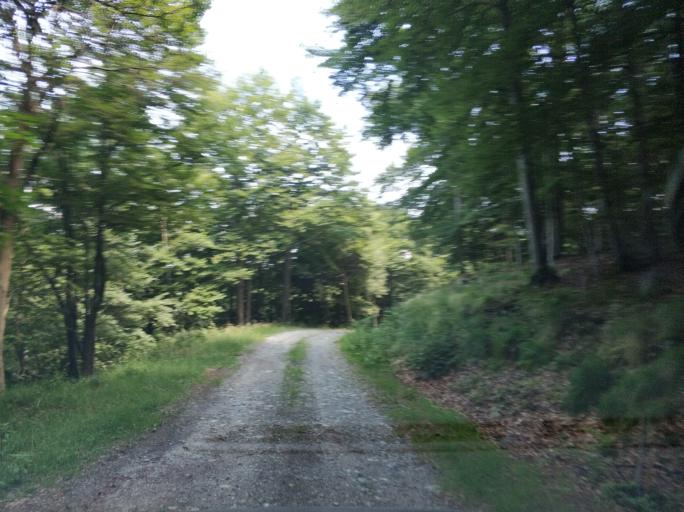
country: IT
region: Piedmont
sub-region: Provincia di Torino
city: Ceres
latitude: 45.3116
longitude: 7.3616
